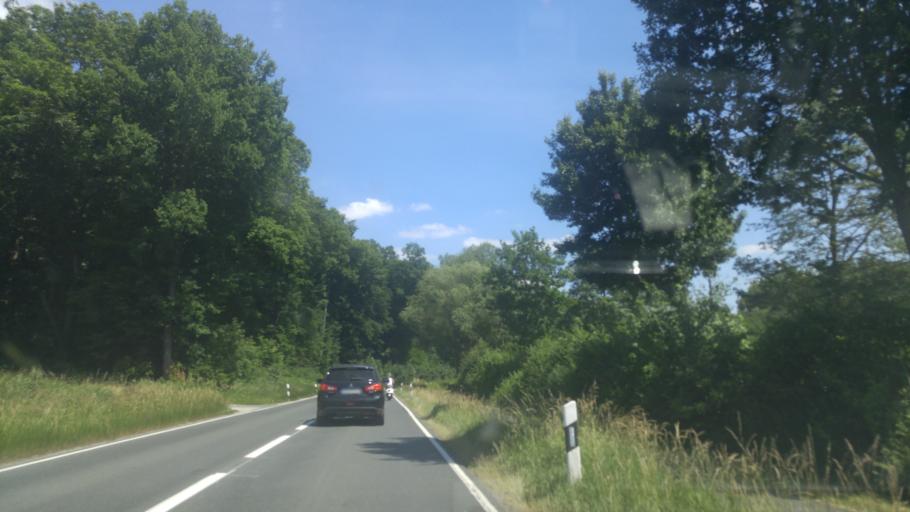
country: DE
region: Bavaria
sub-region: Regierungsbezirk Mittelfranken
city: Herzogenaurach
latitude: 49.5759
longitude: 10.8575
